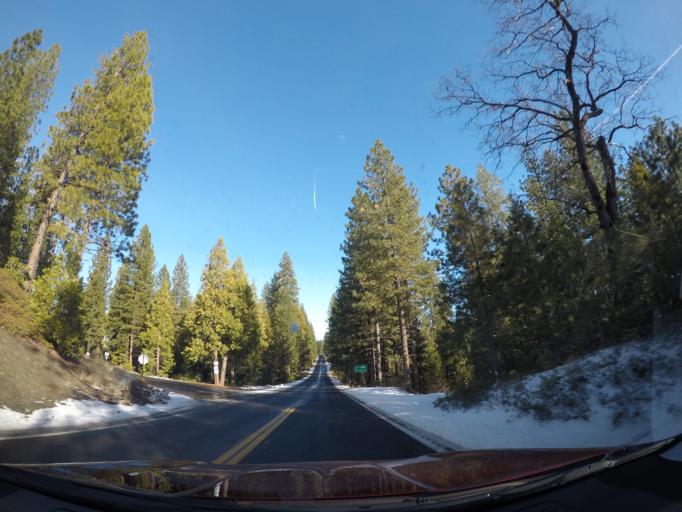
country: US
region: California
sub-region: Tuolumne County
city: Twain Harte
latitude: 38.1696
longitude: -120.0401
